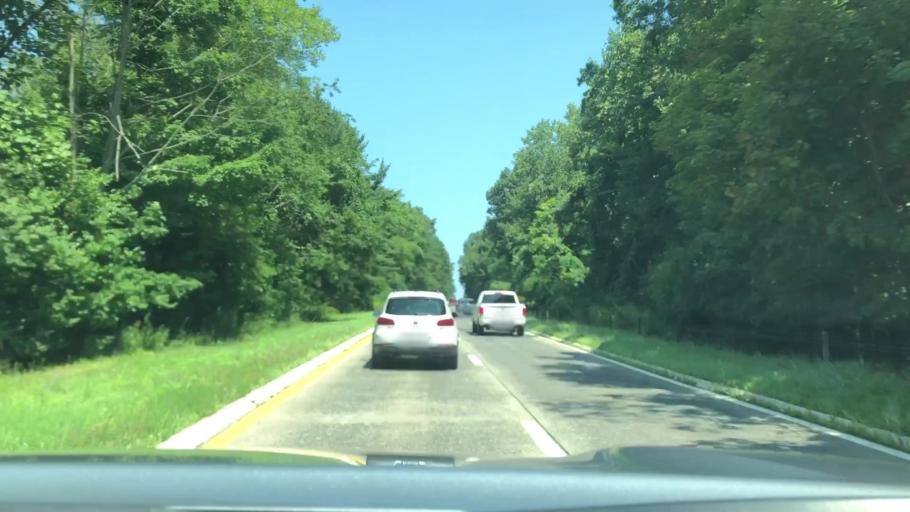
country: US
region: New York
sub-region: Rockland County
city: New Hempstead
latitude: 41.1536
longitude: -74.0264
